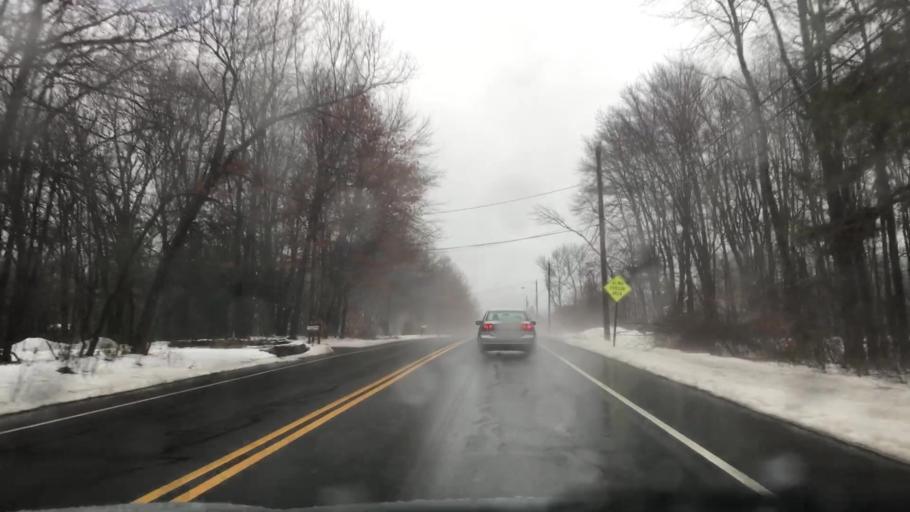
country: US
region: Massachusetts
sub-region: Hampden County
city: Ludlow
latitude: 42.1984
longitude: -72.4967
